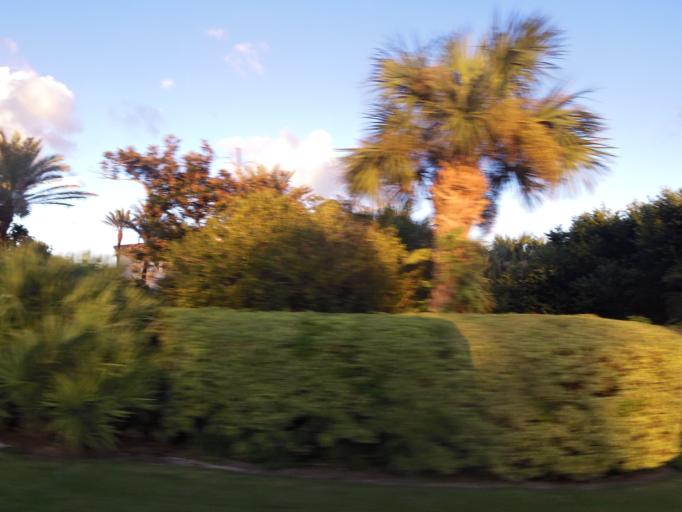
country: US
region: Florida
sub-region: Saint Johns County
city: Sawgrass
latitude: 30.1842
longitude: -81.3629
